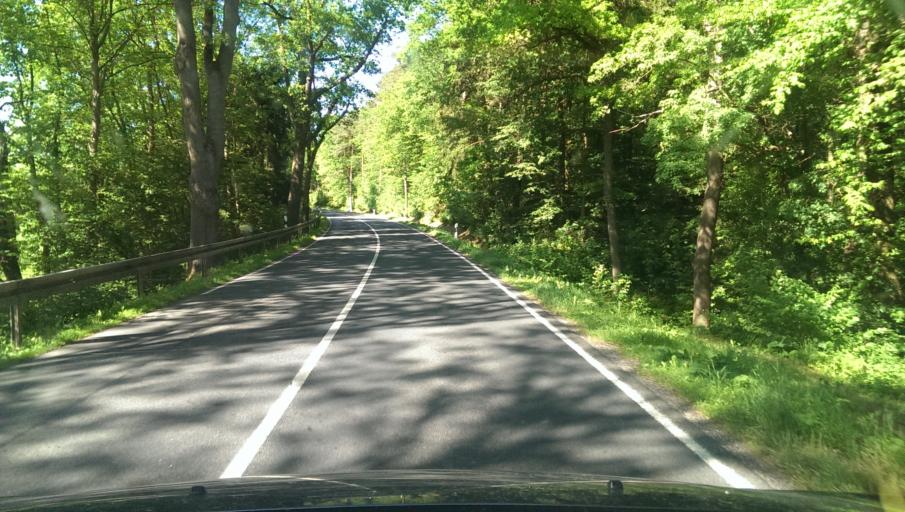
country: DE
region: Thuringia
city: Barchfeld
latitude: 50.8170
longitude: 11.1821
